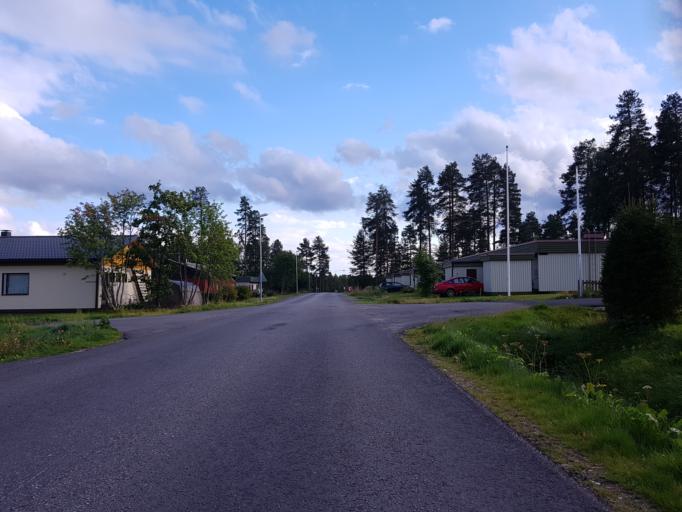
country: FI
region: Kainuu
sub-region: Kehys-Kainuu
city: Kuhmo
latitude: 64.1194
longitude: 29.5356
